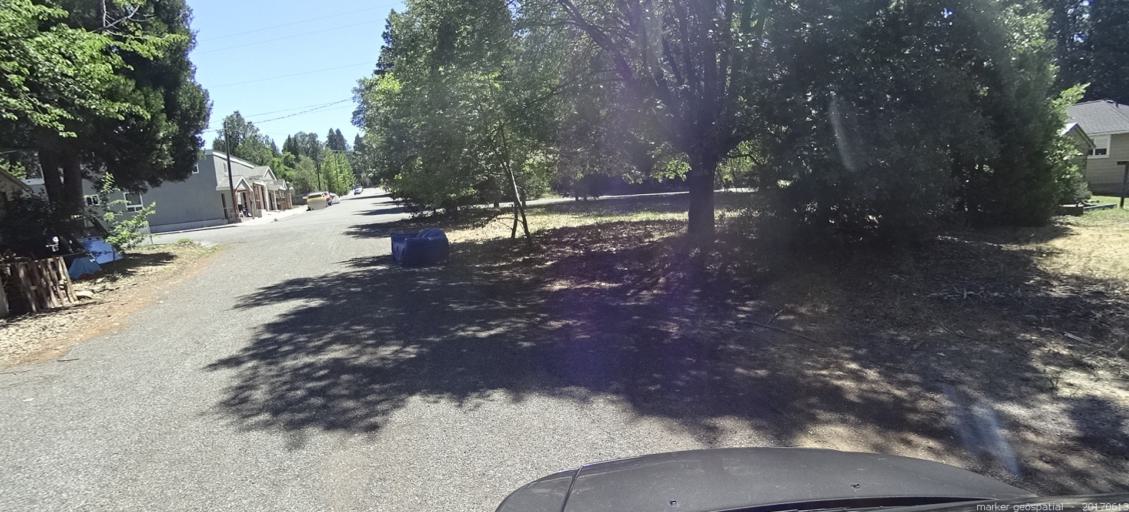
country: US
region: California
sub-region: Siskiyou County
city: Mount Shasta
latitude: 41.3099
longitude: -122.3140
